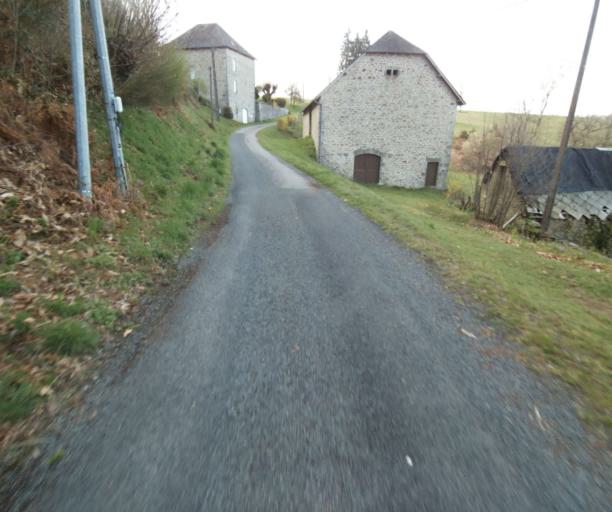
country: FR
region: Limousin
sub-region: Departement de la Correze
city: Correze
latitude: 45.3645
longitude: 1.8516
